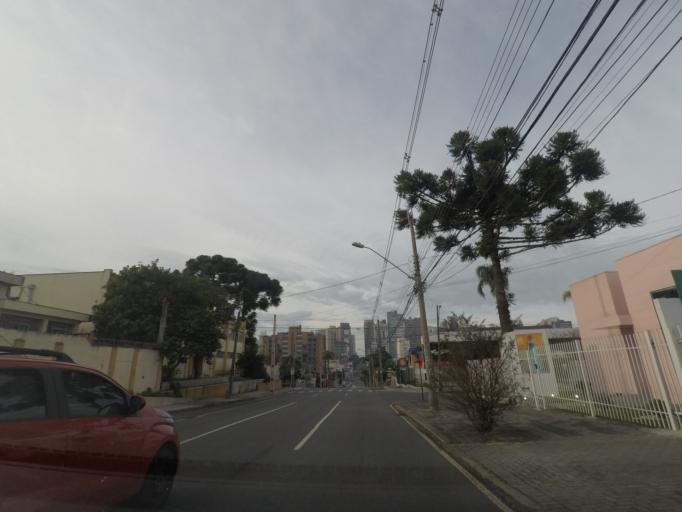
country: BR
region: Parana
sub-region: Curitiba
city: Curitiba
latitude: -25.4396
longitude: -49.2908
